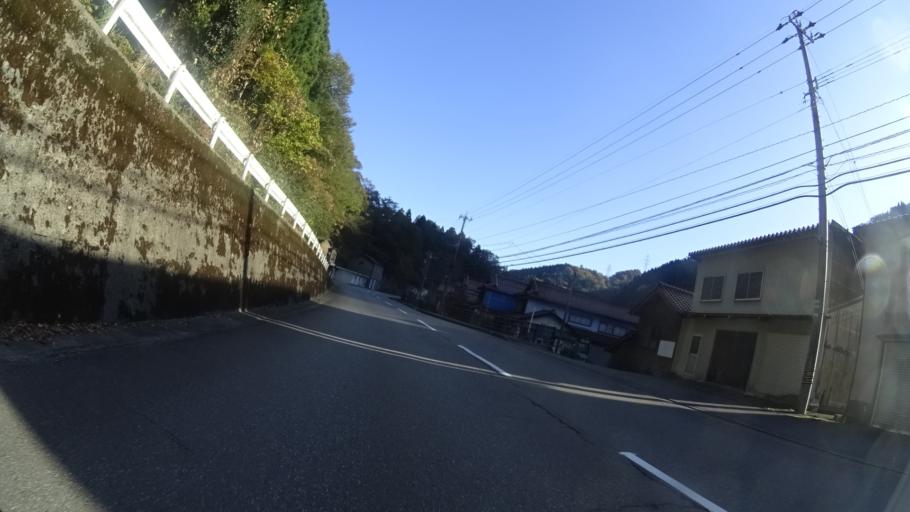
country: JP
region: Fukui
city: Maruoka
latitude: 36.2231
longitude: 136.3581
